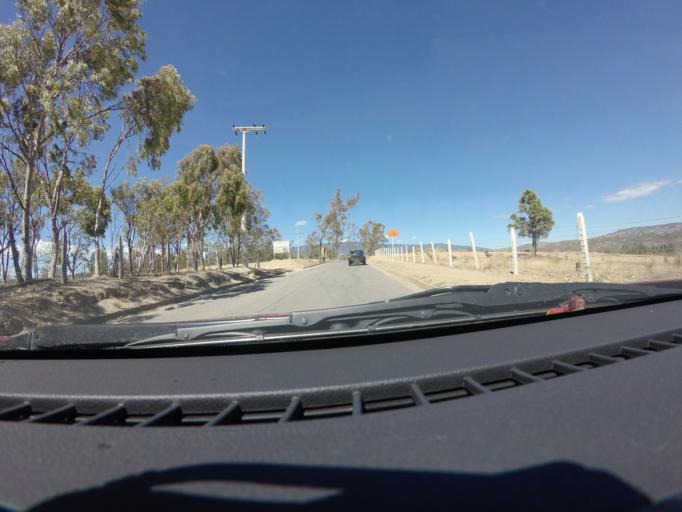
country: CO
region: Boyaca
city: Villa de Leiva
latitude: 5.6294
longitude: -73.5433
